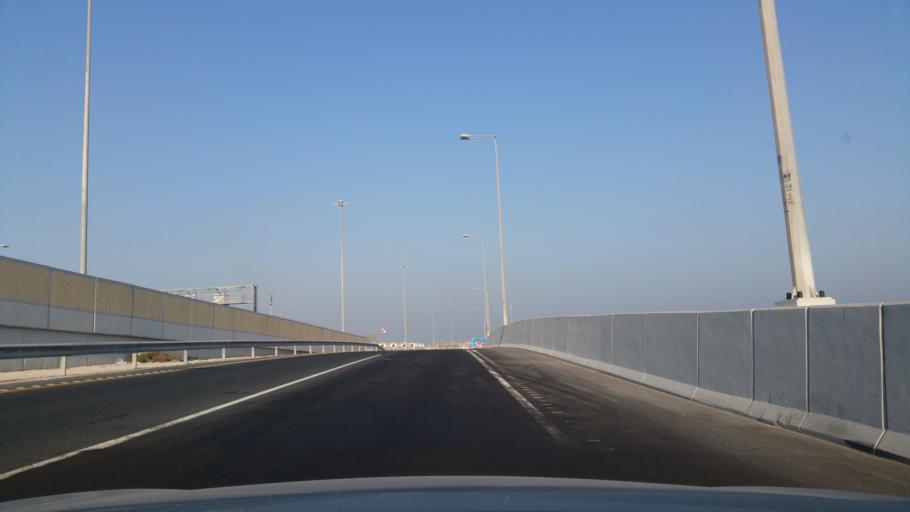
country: QA
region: Al Wakrah
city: Al Wakrah
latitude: 25.1633
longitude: 51.5699
